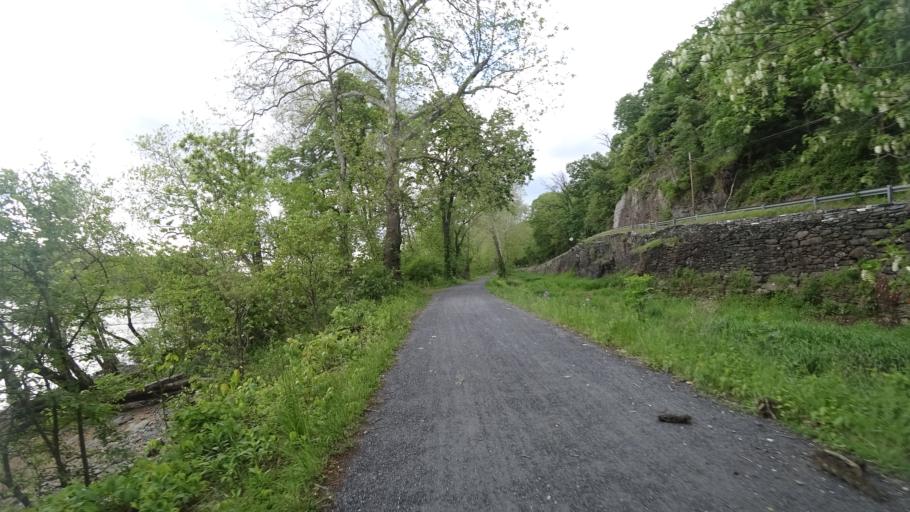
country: US
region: West Virginia
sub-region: Jefferson County
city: Bolivar
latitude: 39.3307
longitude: -77.7352
